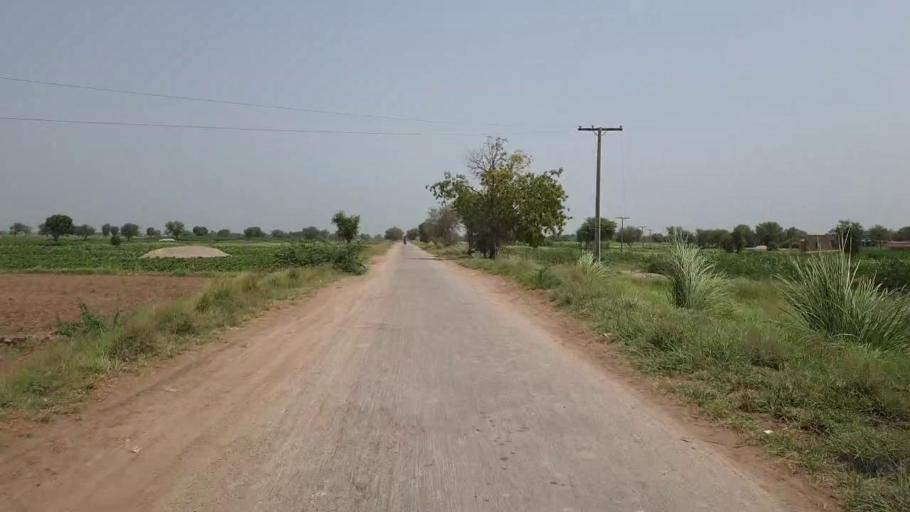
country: PK
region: Sindh
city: Nawabshah
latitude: 26.2597
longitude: 68.3193
